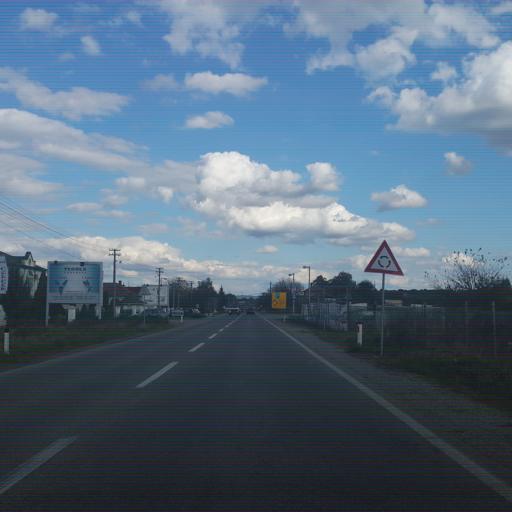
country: RS
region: Central Serbia
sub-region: Rasinski Okrug
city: Krusevac
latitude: 43.5854
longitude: 21.2435
